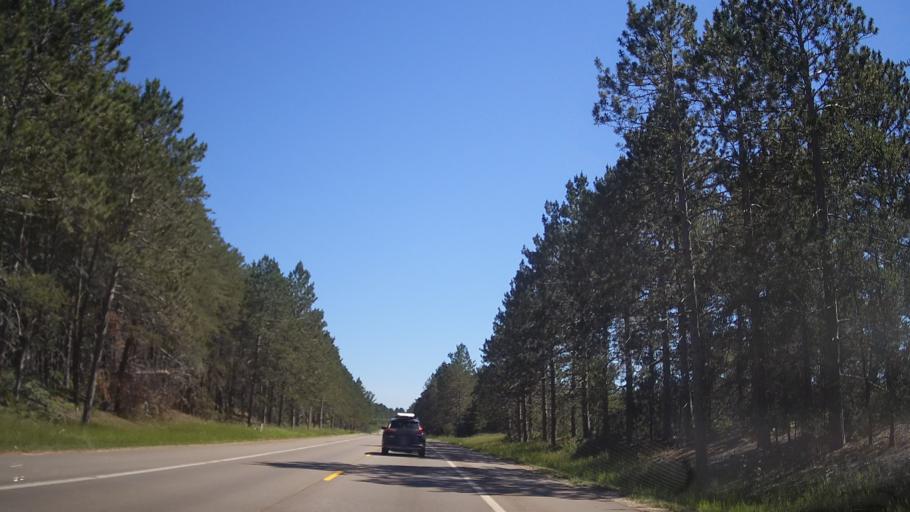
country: US
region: Michigan
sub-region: Cheboygan County
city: Indian River
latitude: 45.5444
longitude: -84.7841
